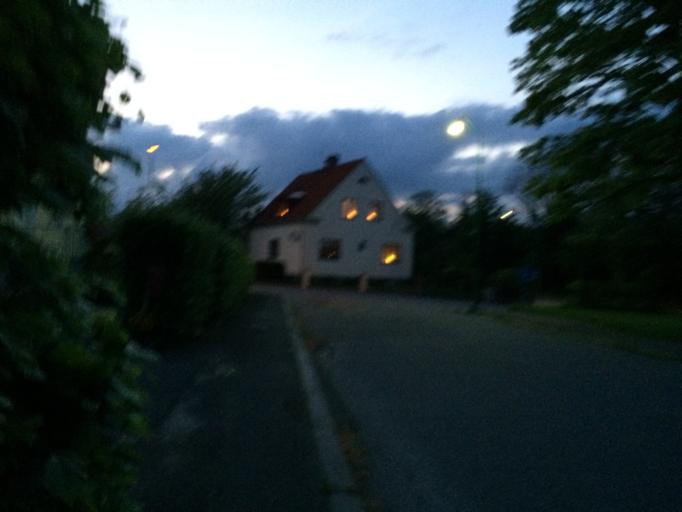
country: SE
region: Skane
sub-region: Simrishamns Kommun
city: Simrishamn
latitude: 55.5598
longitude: 14.3419
